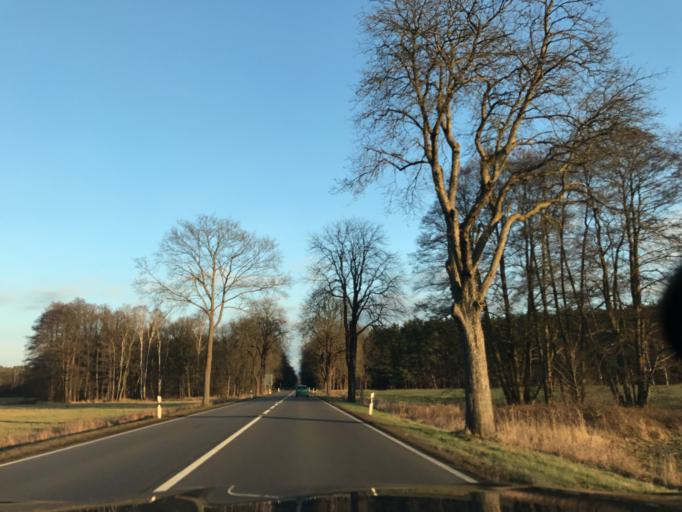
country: DE
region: Saxony-Anhalt
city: Genthin
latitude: 52.4104
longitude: 12.2090
